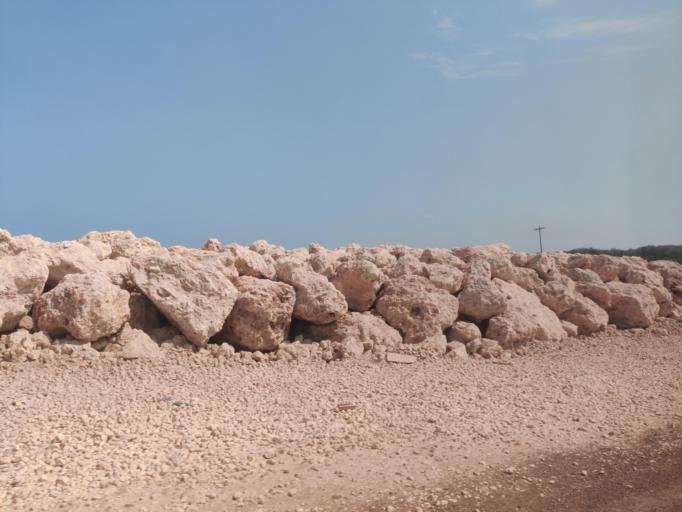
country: CO
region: Bolivar
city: Turbana
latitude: 10.1897
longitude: -75.6353
